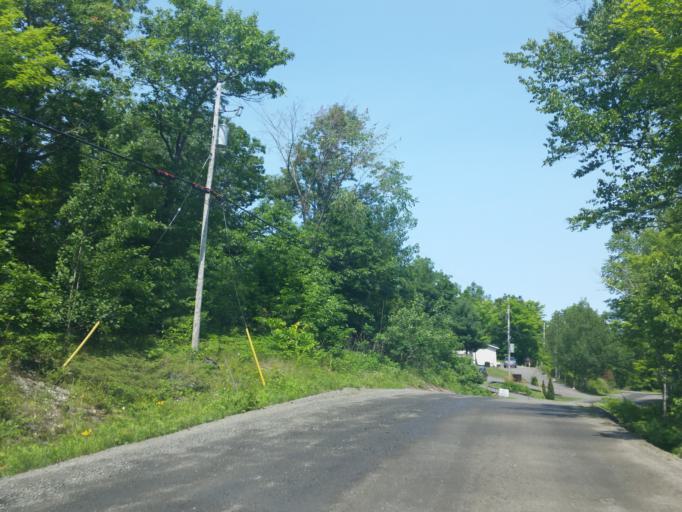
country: CA
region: Ontario
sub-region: Parry Sound District
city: Parry Sound
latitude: 45.4310
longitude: -80.0107
